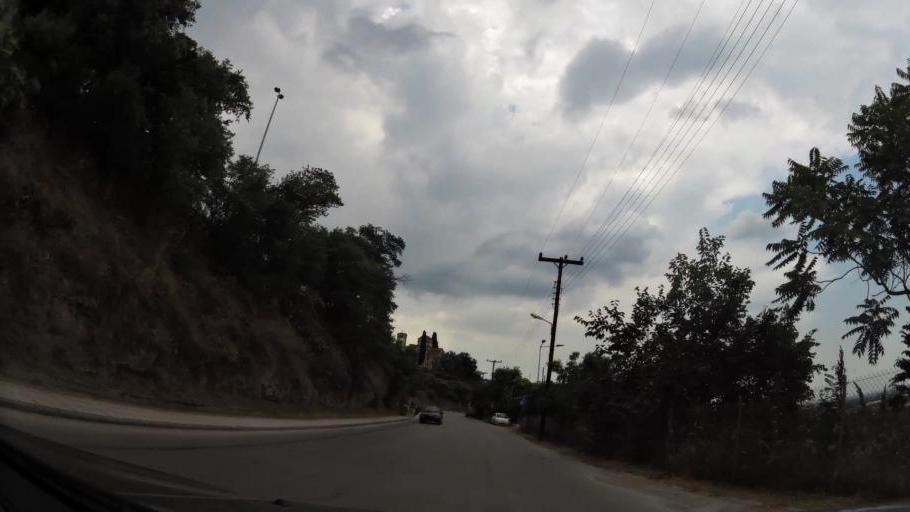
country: GR
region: Central Macedonia
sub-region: Nomos Imathias
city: Veroia
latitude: 40.5235
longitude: 22.2086
